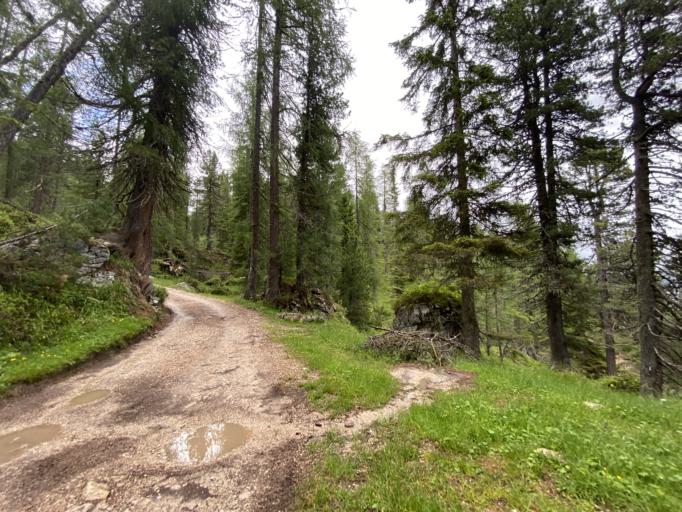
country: IT
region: Veneto
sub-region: Provincia di Belluno
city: Cortina d'Ampezzo
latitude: 46.4842
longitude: 12.1102
